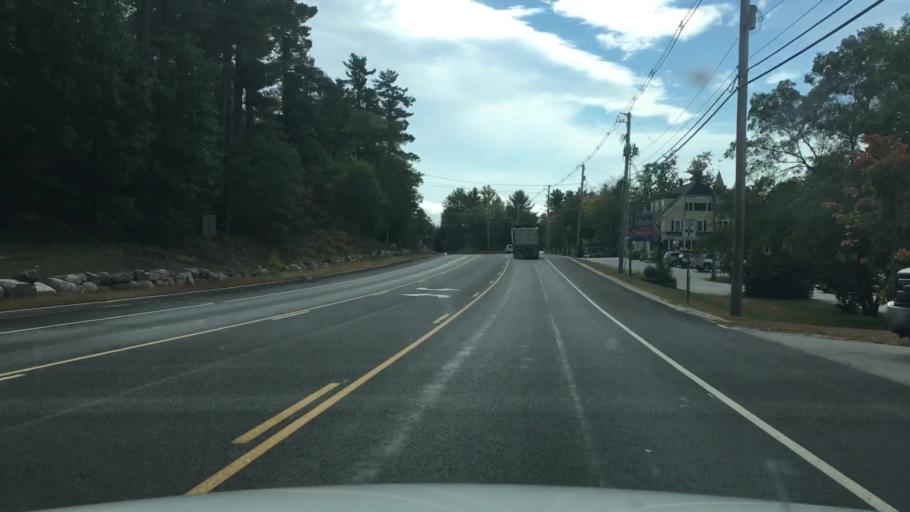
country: US
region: New Hampshire
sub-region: Carroll County
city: North Conway
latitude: 44.0696
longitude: -71.1430
